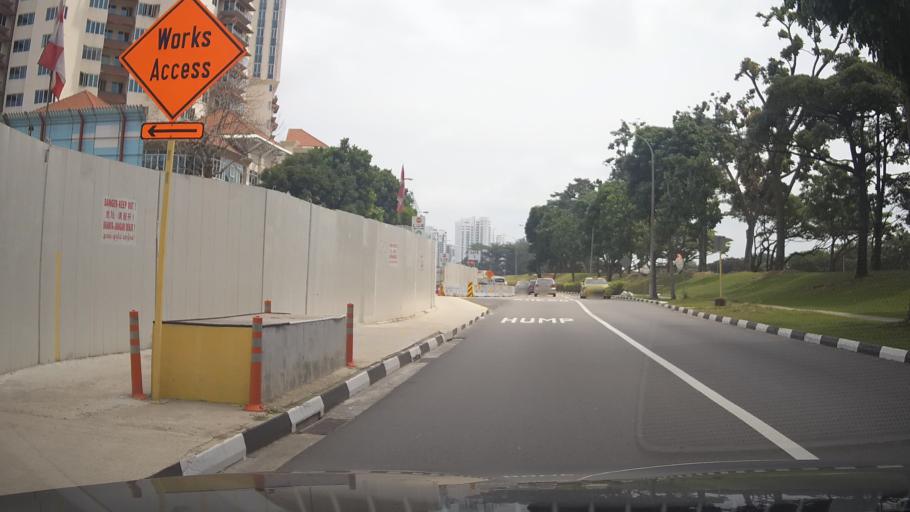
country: SG
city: Singapore
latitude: 1.2966
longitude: 103.8735
